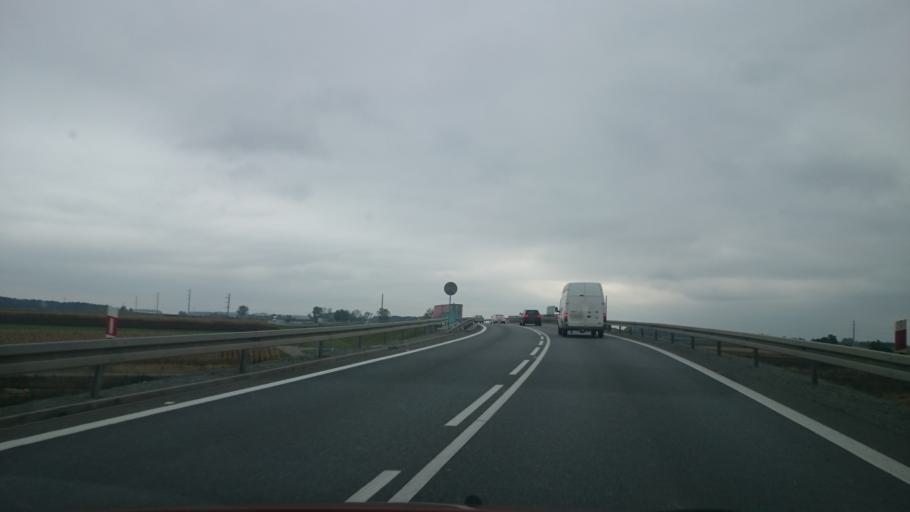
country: PL
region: Lower Silesian Voivodeship
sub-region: Powiat wroclawski
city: Kobierzyce
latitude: 50.9997
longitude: 16.9468
